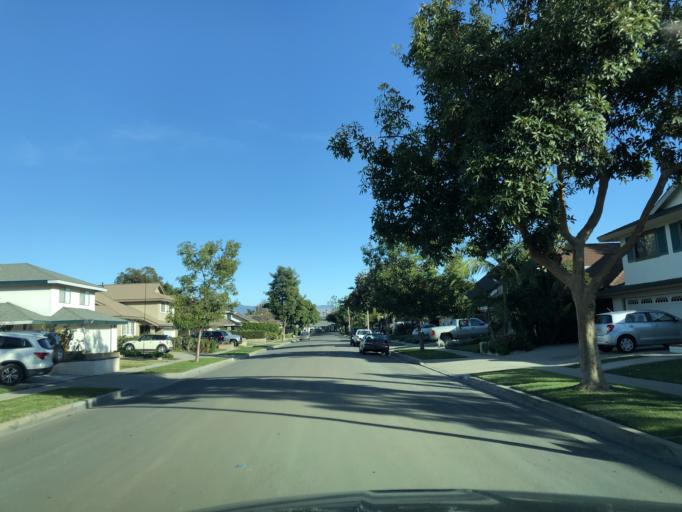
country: US
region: California
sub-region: Orange County
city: Tustin
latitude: 33.7639
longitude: -117.8417
